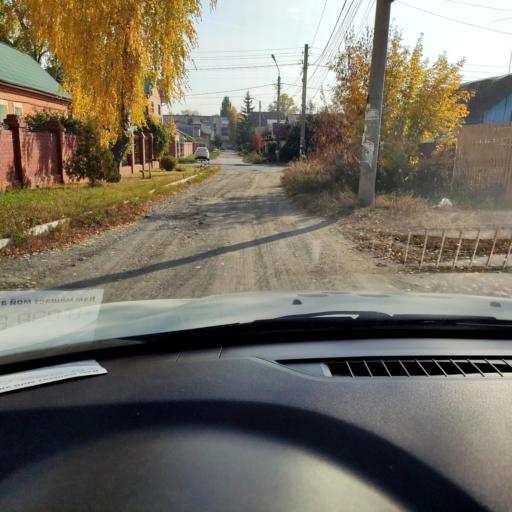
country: RU
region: Samara
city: Tol'yatti
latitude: 53.5322
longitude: 49.3993
